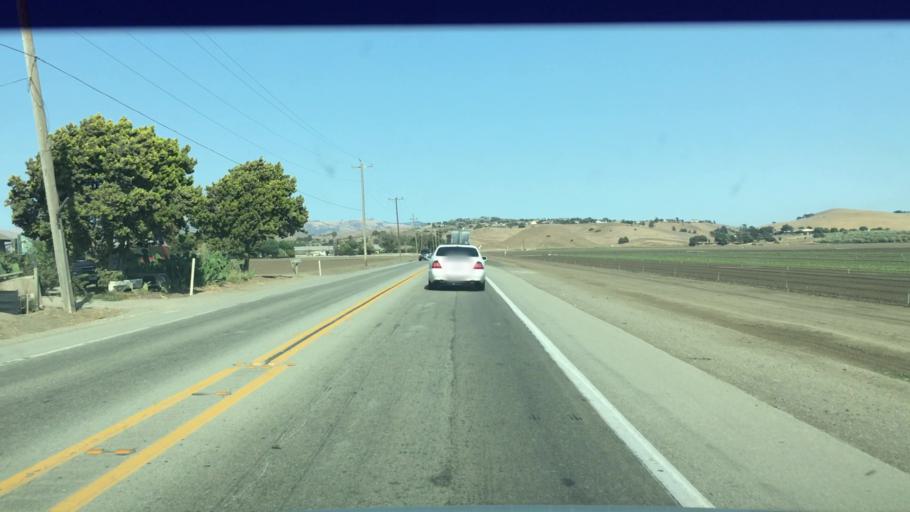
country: US
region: California
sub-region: San Benito County
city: San Juan Bautista
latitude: 36.8418
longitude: -121.4706
